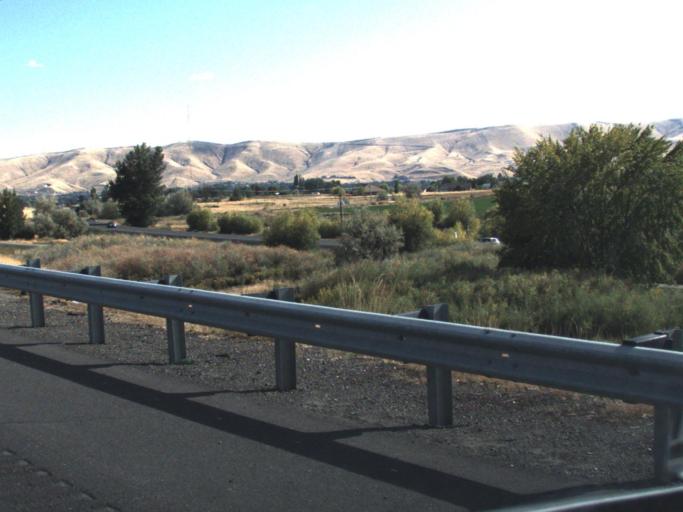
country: US
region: Washington
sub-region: Benton County
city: Prosser
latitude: 46.2384
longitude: -119.8196
